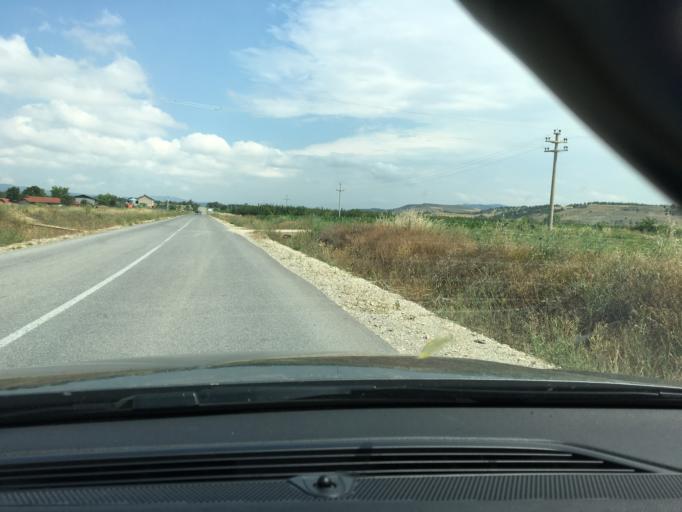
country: MK
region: Sveti Nikole
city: Sveti Nikole
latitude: 41.8804
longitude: 21.9396
